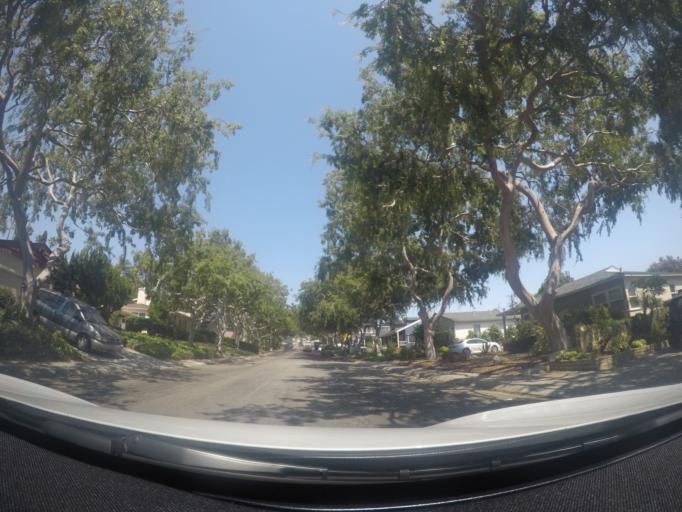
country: US
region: California
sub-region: Los Angeles County
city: Palos Verdes Estates
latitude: 33.8200
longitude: -118.3671
